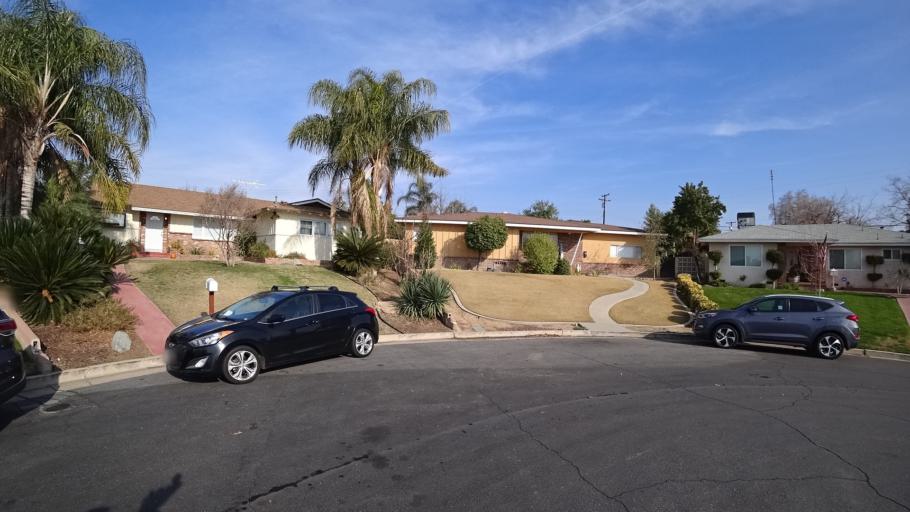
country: US
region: California
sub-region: Kern County
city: Oildale
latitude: 35.4031
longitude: -118.9755
